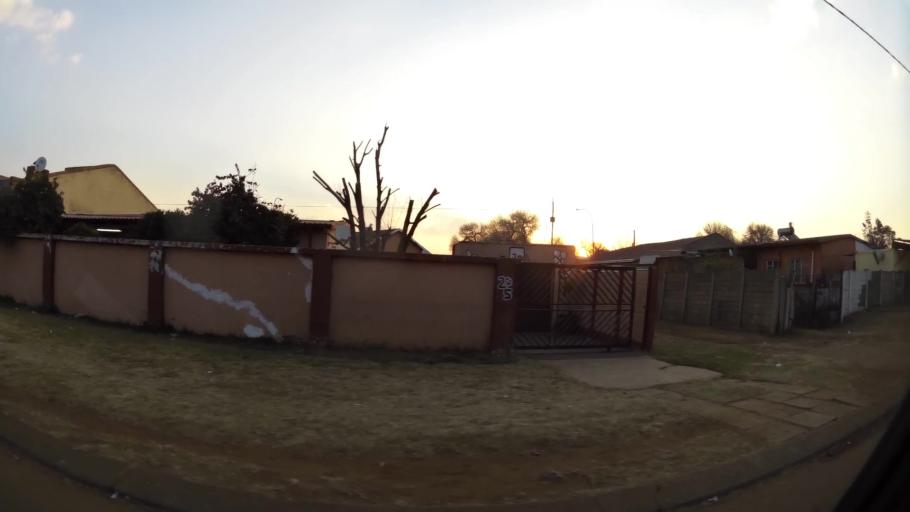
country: ZA
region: Gauteng
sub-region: City of Johannesburg Metropolitan Municipality
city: Soweto
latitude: -26.2855
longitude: 27.8918
